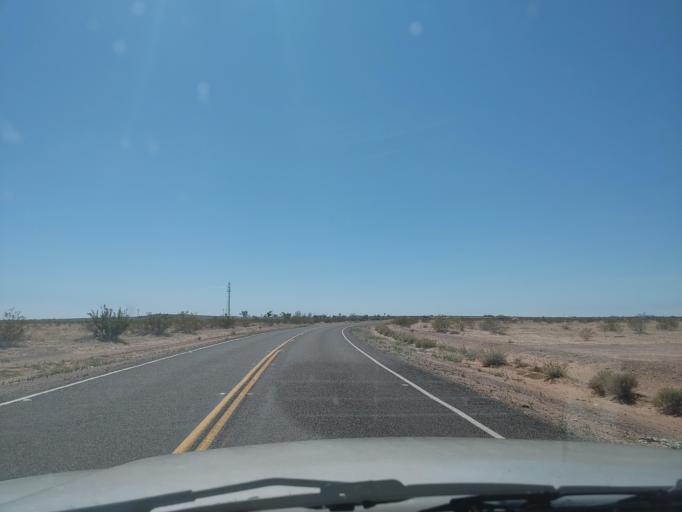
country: US
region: Arizona
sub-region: Maricopa County
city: Gila Bend
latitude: 32.8706
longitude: -113.2132
